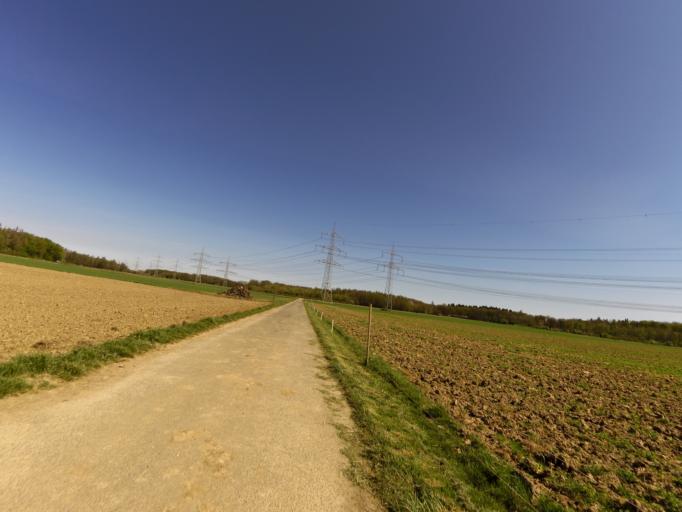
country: DE
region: North Rhine-Westphalia
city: Meckenheim
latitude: 50.6576
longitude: 7.0065
